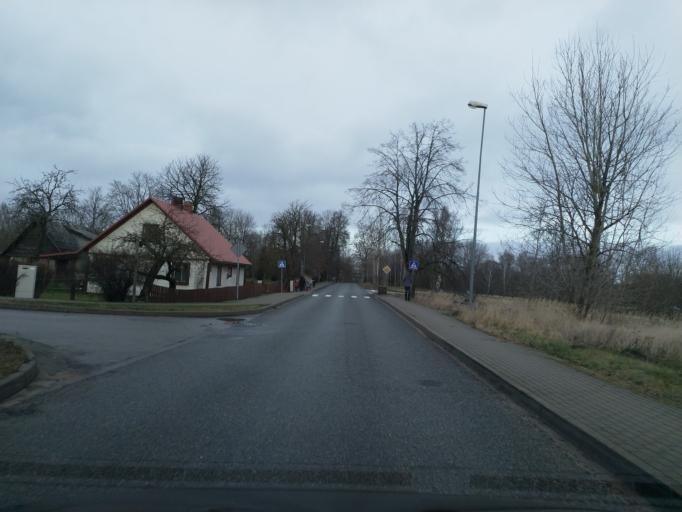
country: LV
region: Kuldigas Rajons
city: Kuldiga
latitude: 56.9592
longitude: 21.9733
